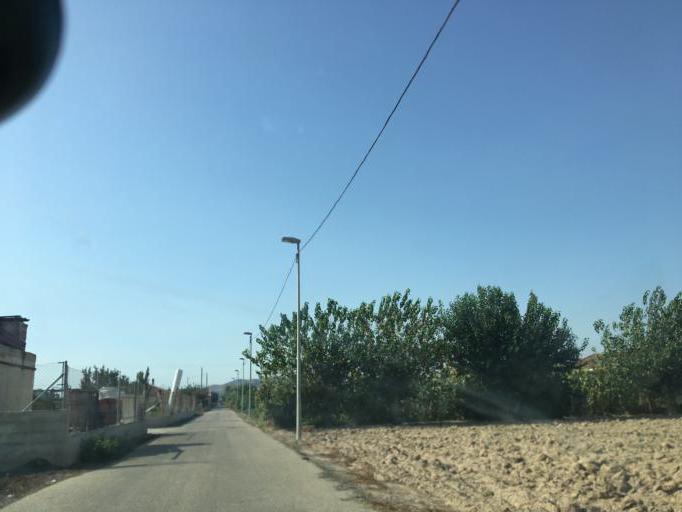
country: ES
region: Murcia
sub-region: Murcia
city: Santomera
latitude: 38.0244
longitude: -1.0531
